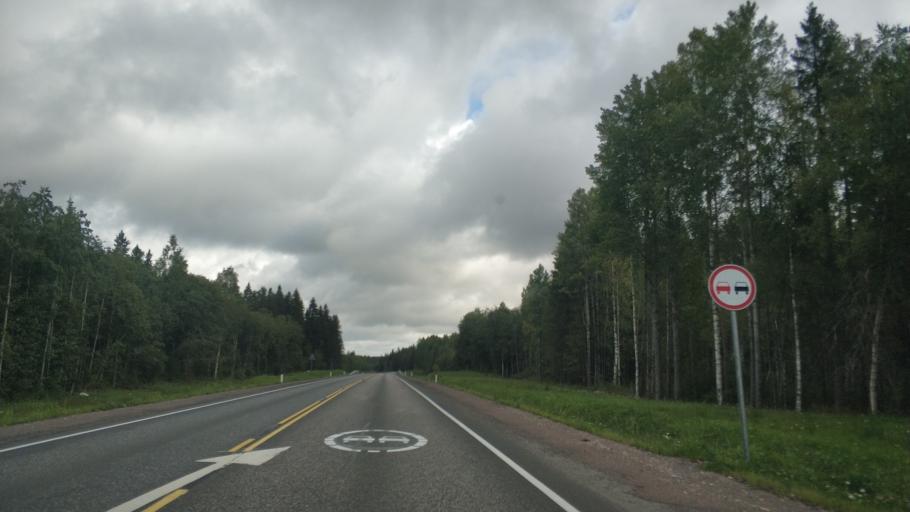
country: RU
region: Republic of Karelia
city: Khelyulya
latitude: 61.8442
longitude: 30.6470
